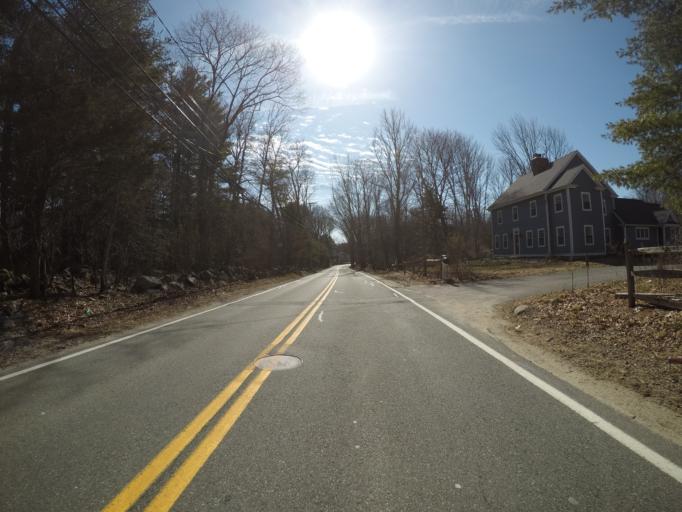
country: US
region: Massachusetts
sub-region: Norfolk County
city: Stoughton
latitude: 42.1032
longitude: -71.1315
